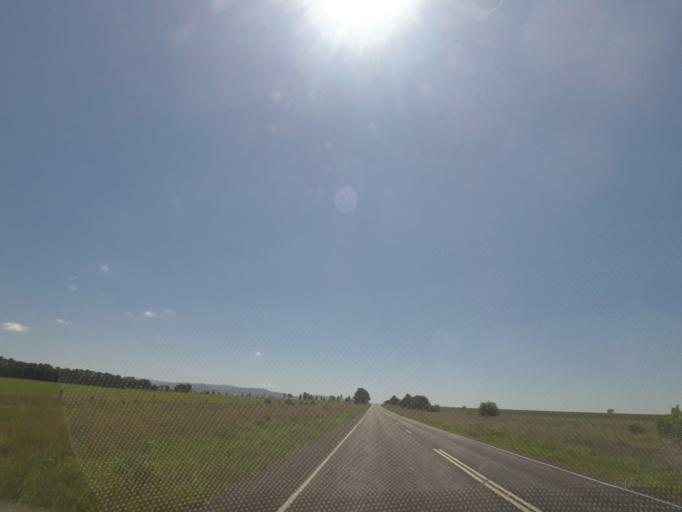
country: AU
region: Victoria
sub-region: Hume
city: Sunbury
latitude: -37.4866
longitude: 144.7545
